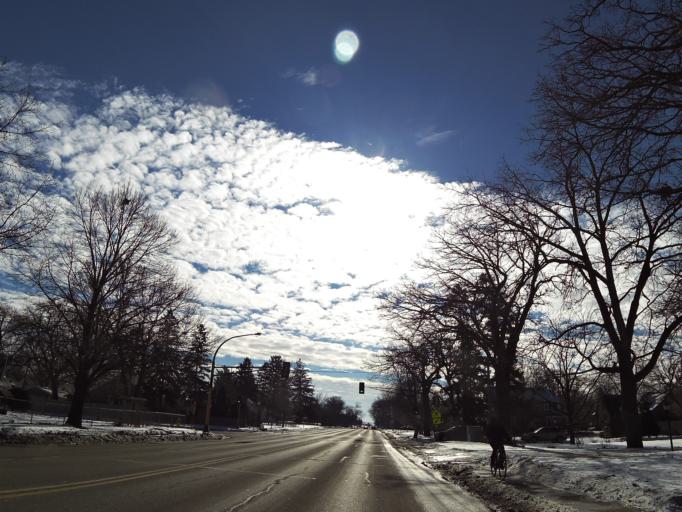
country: US
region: Minnesota
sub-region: Hennepin County
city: Richfield
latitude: 44.8714
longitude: -93.2885
